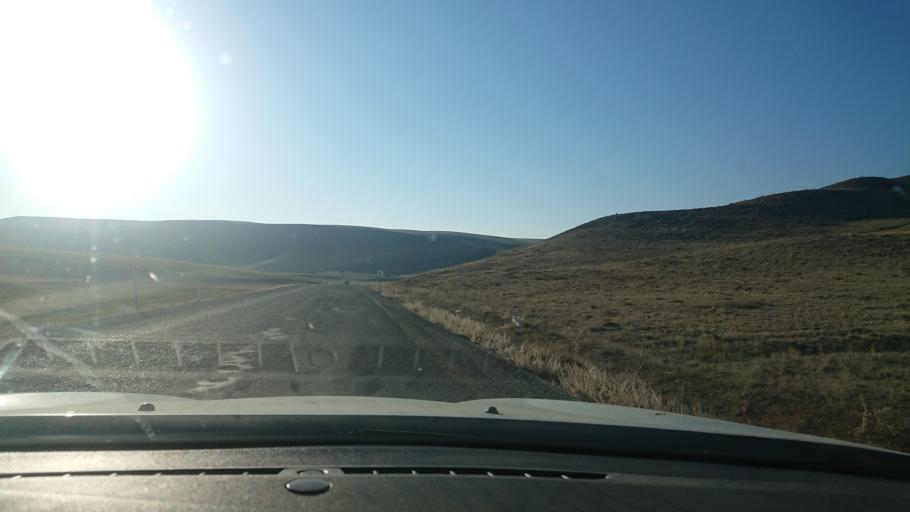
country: TR
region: Aksaray
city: Acipinar
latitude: 38.7114
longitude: 33.7682
